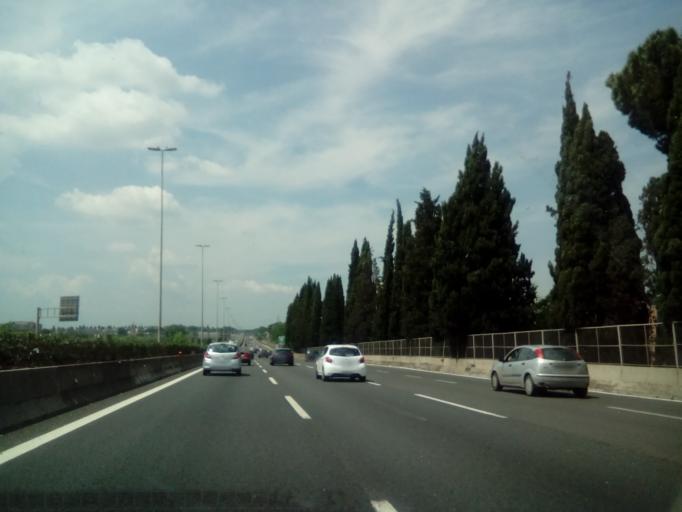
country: IT
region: Latium
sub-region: Citta metropolitana di Roma Capitale
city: Colle Verde
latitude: 41.9344
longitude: 12.6005
